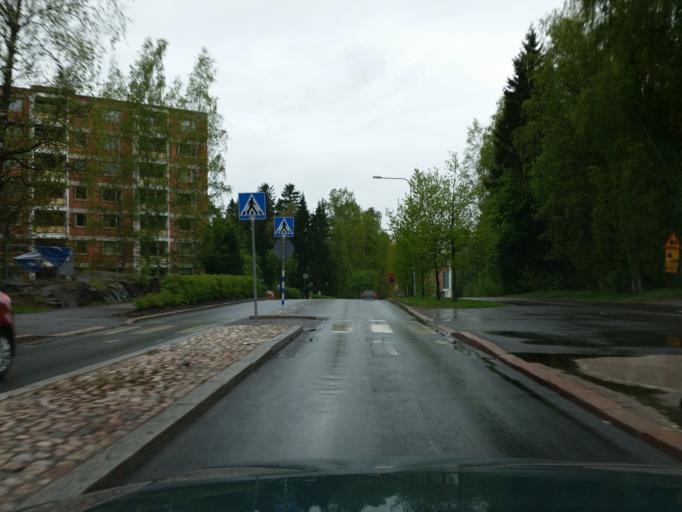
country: FI
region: Uusimaa
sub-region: Helsinki
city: Teekkarikylae
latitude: 60.2312
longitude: 24.8923
